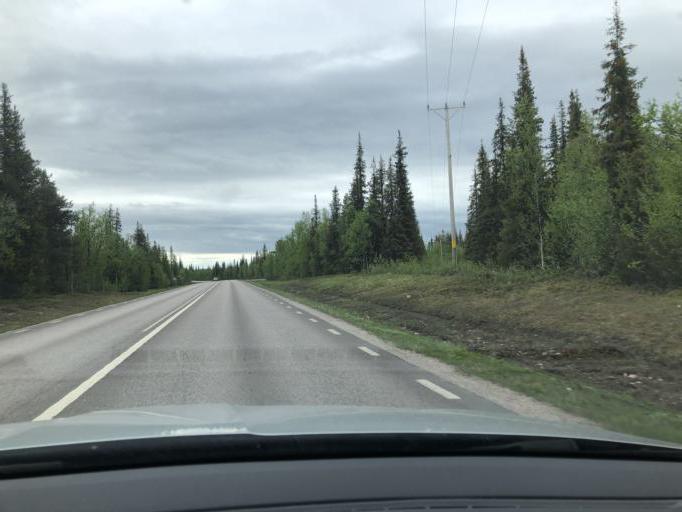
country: SE
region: Norrbotten
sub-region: Kiruna Kommun
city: Kiruna
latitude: 67.7503
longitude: 20.6415
